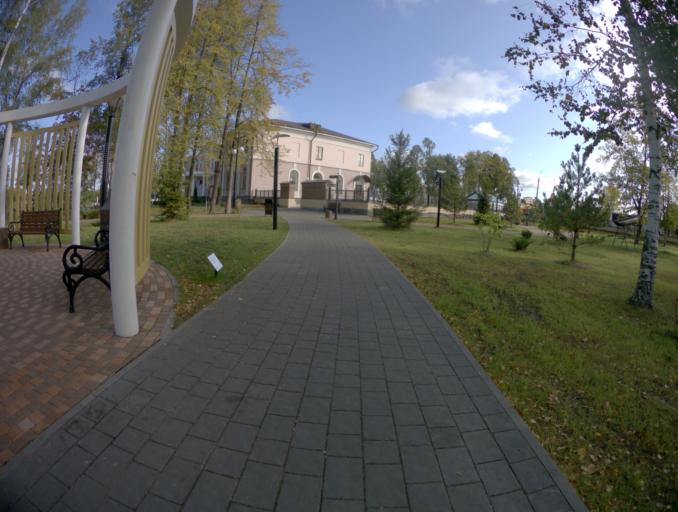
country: RU
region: Moskovskaya
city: Roshal'
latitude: 55.6601
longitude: 39.8670
